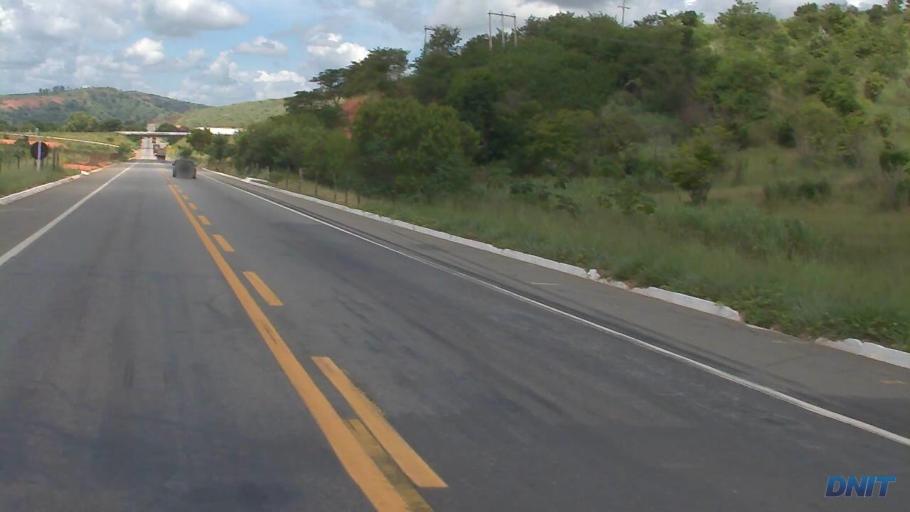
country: BR
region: Minas Gerais
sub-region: Governador Valadares
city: Governador Valadares
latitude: -18.9235
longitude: -42.0228
